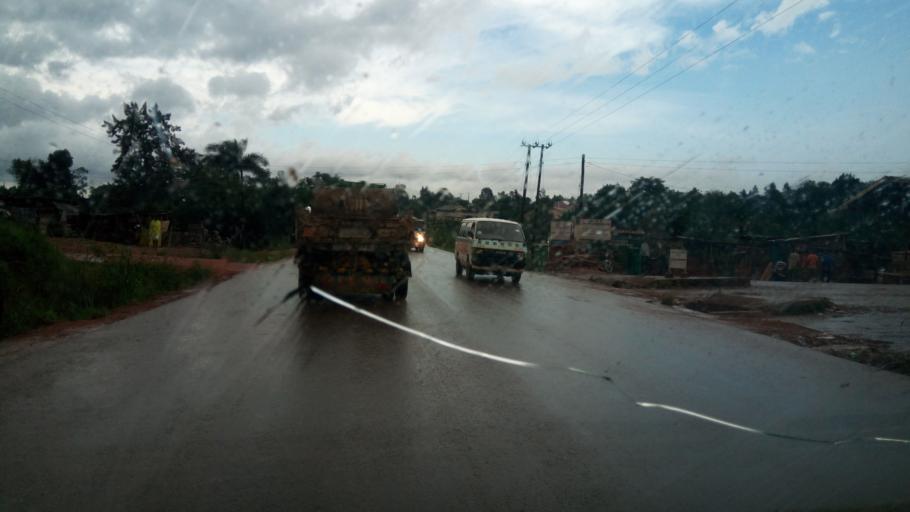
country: UG
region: Central Region
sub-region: Wakiso District
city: Wakiso
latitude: 0.3971
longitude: 32.4879
